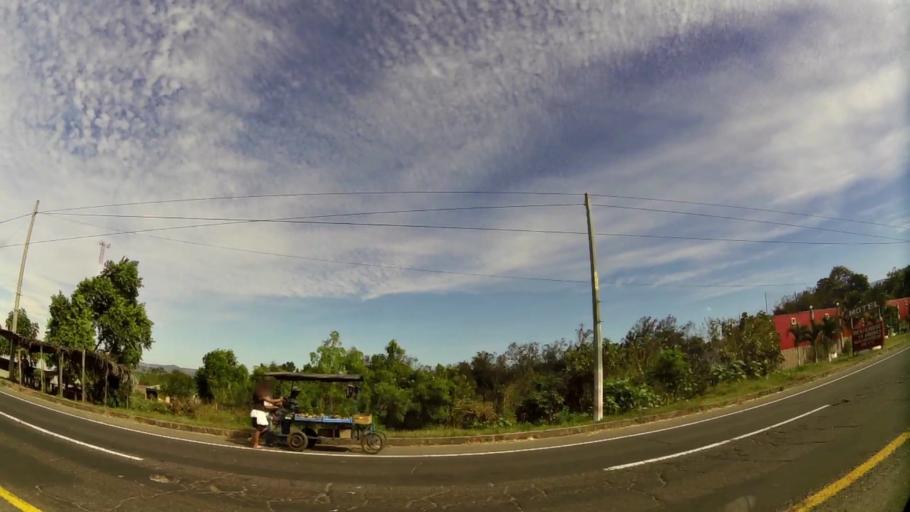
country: SV
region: Santa Ana
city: Chalchuapa
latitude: 13.9802
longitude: -89.6905
